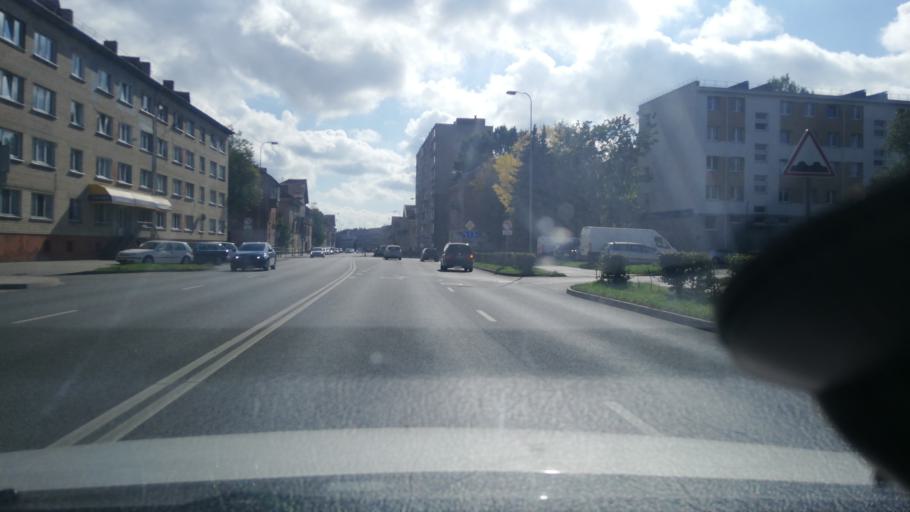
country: LT
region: Klaipedos apskritis
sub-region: Klaipeda
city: Klaipeda
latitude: 55.6815
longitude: 21.1509
